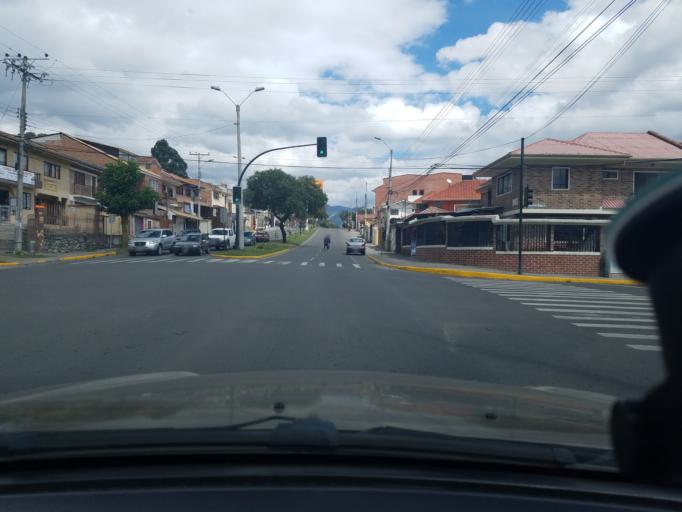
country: EC
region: Azuay
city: Cuenca
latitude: -2.9085
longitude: -79.0168
